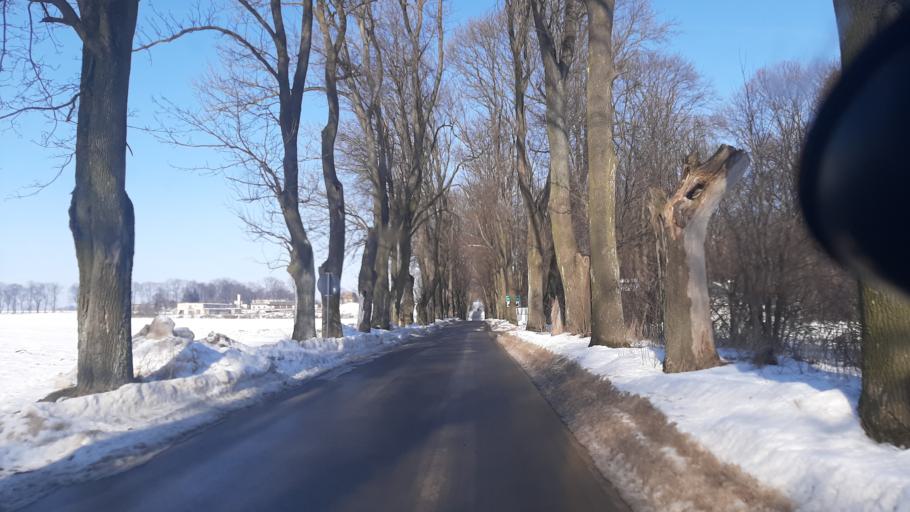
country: PL
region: Lublin Voivodeship
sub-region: Powiat pulawski
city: Naleczow
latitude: 51.3004
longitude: 22.2611
